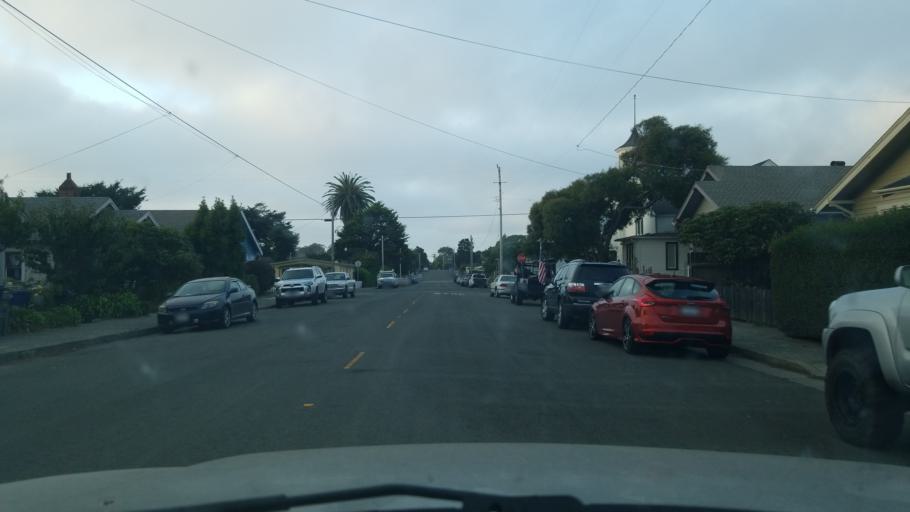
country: US
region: California
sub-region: Mendocino County
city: Fort Bragg
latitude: 39.4447
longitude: -123.7995
